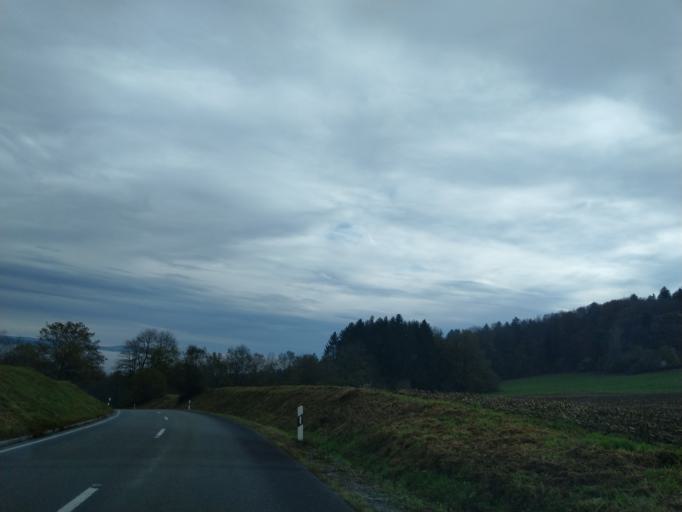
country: DE
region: Bavaria
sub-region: Lower Bavaria
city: Zenting
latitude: 48.7904
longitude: 13.2338
